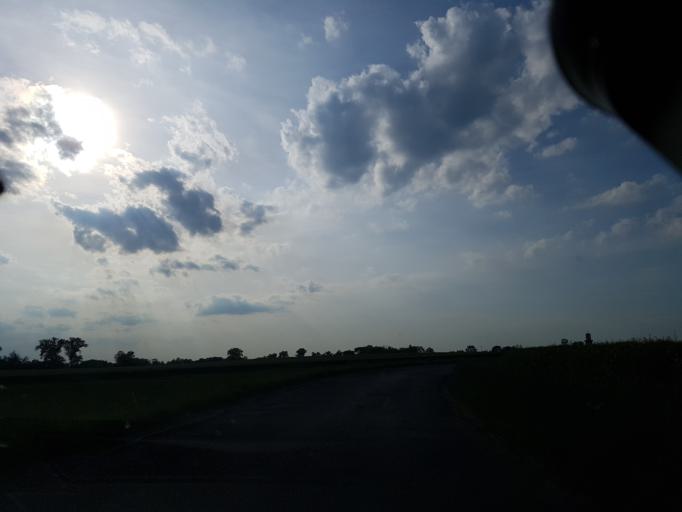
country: PL
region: Lower Silesian Voivodeship
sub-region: Powiat wroclawski
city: Zorawina
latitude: 50.9105
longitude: 17.0031
